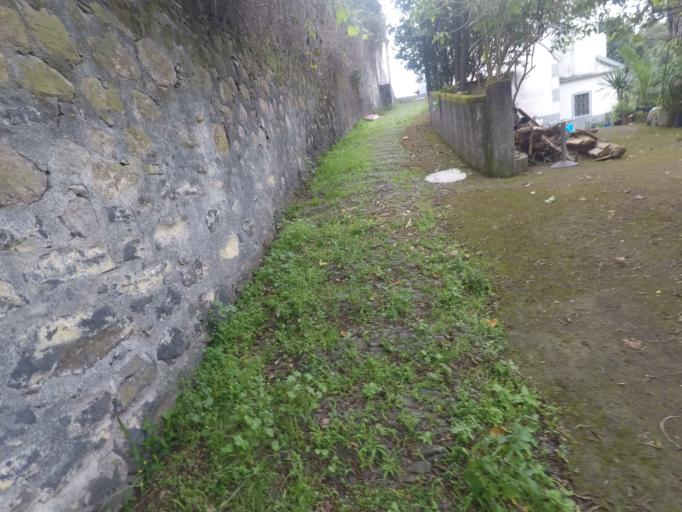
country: PT
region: Madeira
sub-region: Santana
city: Santana
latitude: 32.7589
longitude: -16.8784
